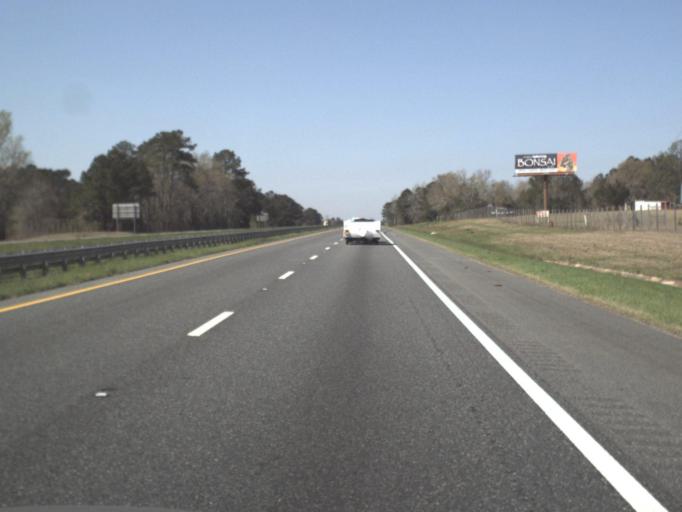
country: US
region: Florida
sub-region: Jackson County
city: Marianna
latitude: 30.7578
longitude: -85.2893
